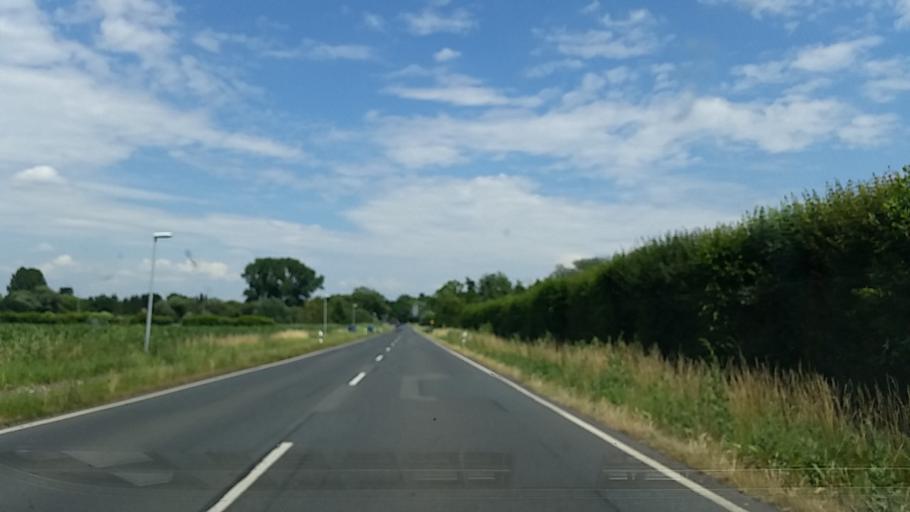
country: DE
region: Lower Saxony
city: Hillerse
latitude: 52.4085
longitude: 10.3930
